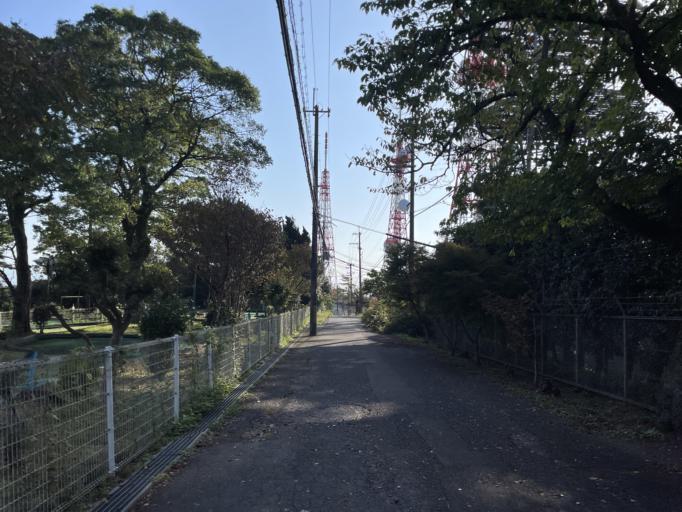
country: JP
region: Nara
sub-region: Ikoma-shi
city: Ikoma
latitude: 34.6768
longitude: 135.6781
